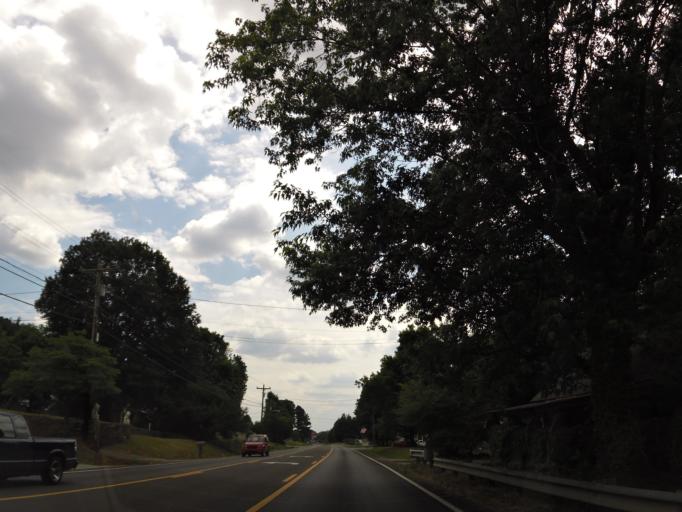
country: US
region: Tennessee
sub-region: Marion County
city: Whitwell
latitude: 35.2078
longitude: -85.5098
